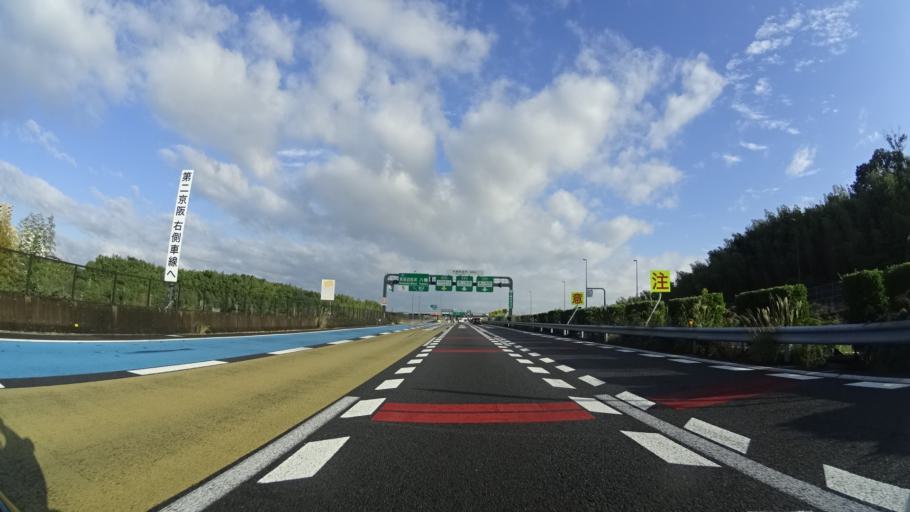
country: JP
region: Kyoto
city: Yawata
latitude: 34.8373
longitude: 135.7235
